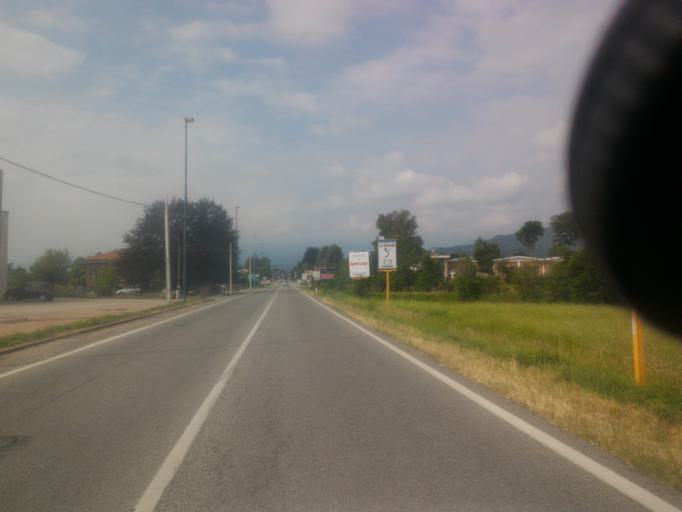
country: IT
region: Piedmont
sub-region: Provincia di Torino
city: Osasco
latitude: 44.8624
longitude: 7.3306
